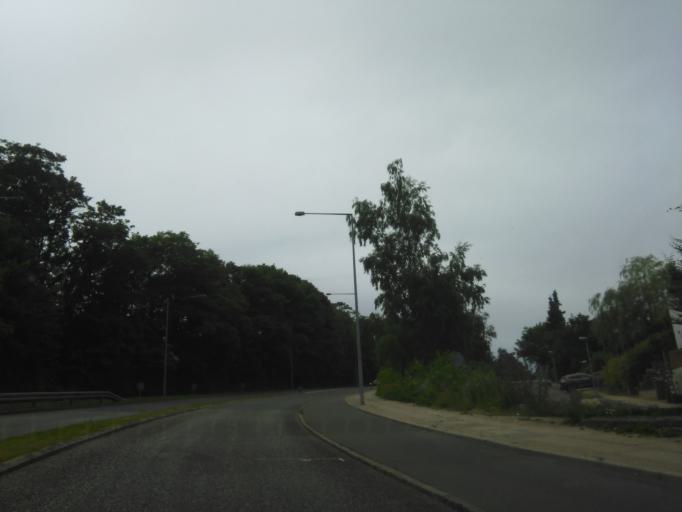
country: DK
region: Central Jutland
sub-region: Horsens Kommune
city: Horsens
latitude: 55.8661
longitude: 9.8925
